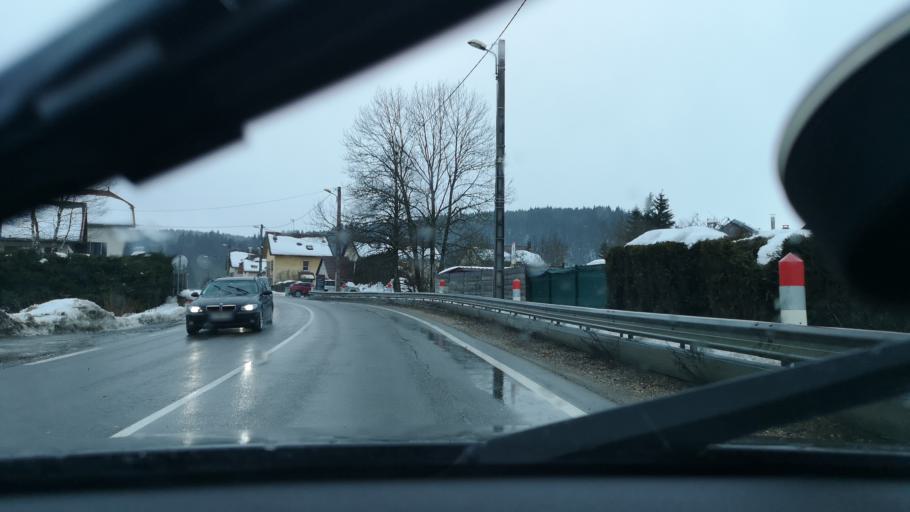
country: FR
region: Franche-Comte
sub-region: Departement du Doubs
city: La Cluse-et-Mijoux
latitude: 46.8673
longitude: 6.3739
